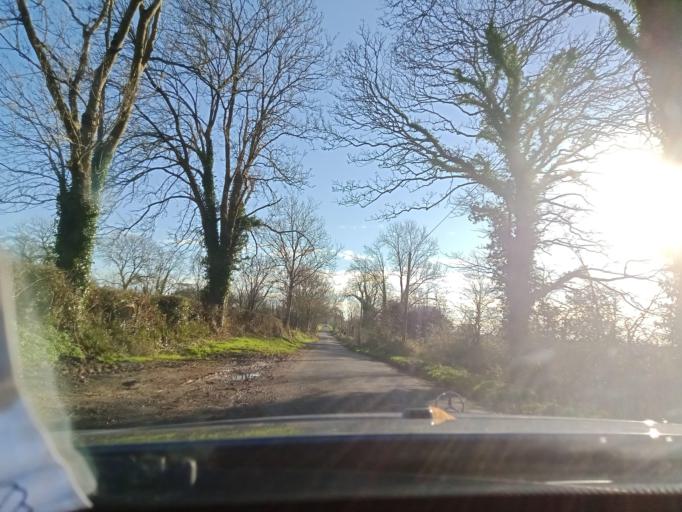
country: IE
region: Leinster
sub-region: Kilkenny
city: Mooncoin
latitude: 52.3404
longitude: -7.2693
